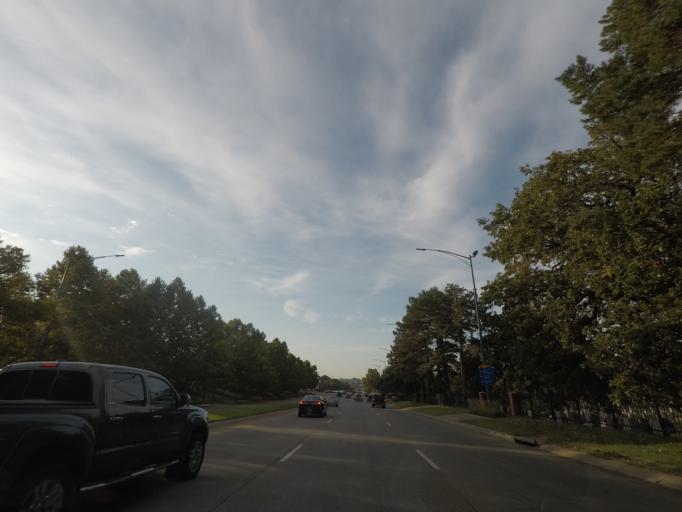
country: US
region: Iowa
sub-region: Polk County
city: Des Moines
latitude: 41.5902
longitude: -93.6449
